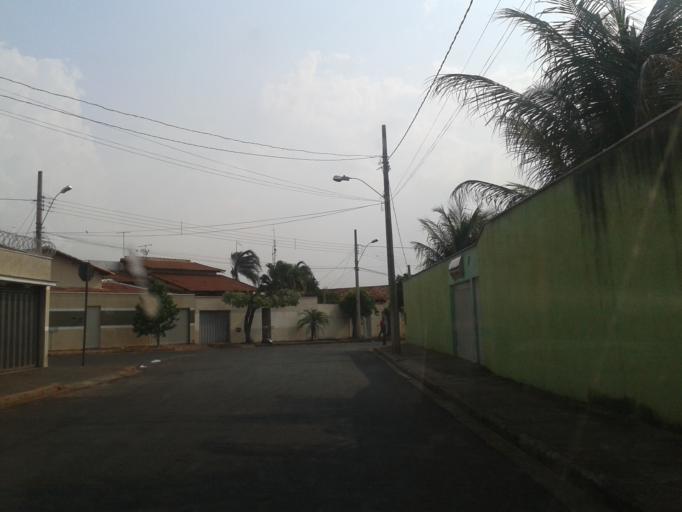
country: BR
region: Minas Gerais
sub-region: Ituiutaba
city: Ituiutaba
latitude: -18.9780
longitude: -49.4838
